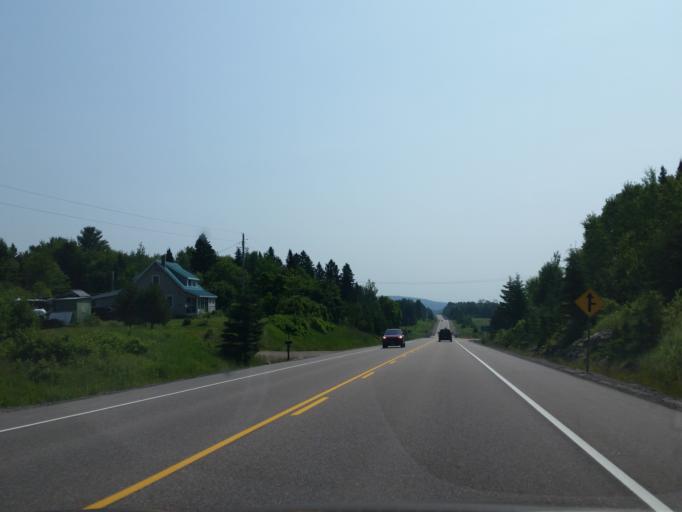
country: CA
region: Ontario
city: Mattawa
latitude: 46.3063
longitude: -78.6262
